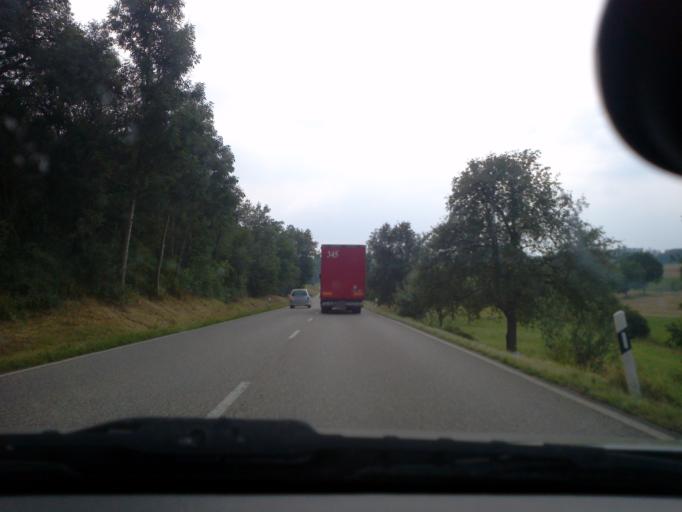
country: DE
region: Baden-Wuerttemberg
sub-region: Karlsruhe Region
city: Gondelsheim
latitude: 49.0366
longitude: 8.6683
